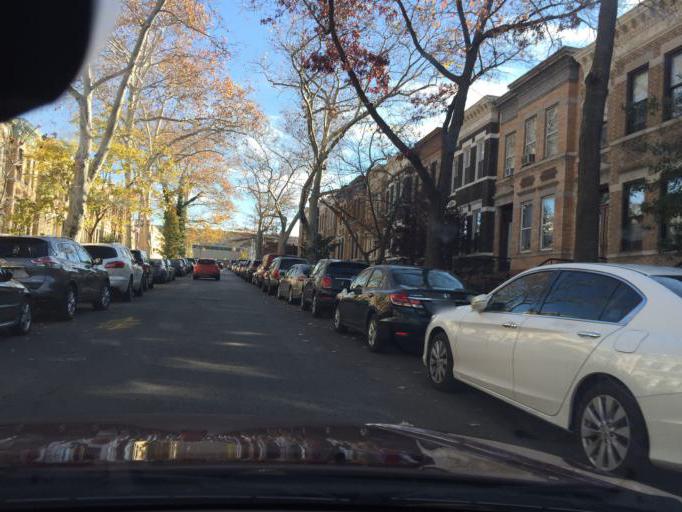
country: US
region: New York
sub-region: Kings County
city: Bensonhurst
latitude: 40.6534
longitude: -74.0043
